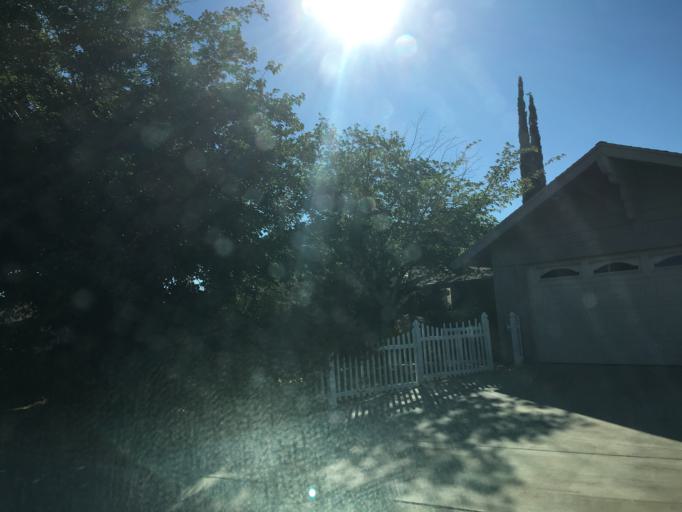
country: US
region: California
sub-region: Los Angeles County
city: Desert View Highlands
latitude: 34.5914
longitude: -118.1551
